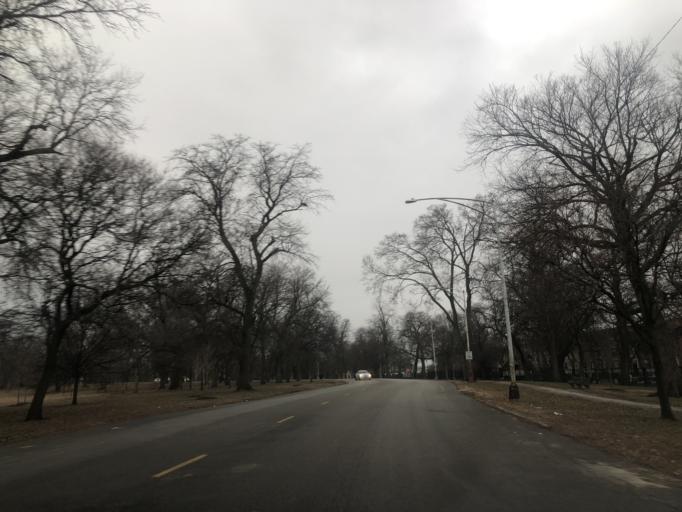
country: US
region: Illinois
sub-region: Cook County
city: Chicago
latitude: 41.7886
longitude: -87.6150
